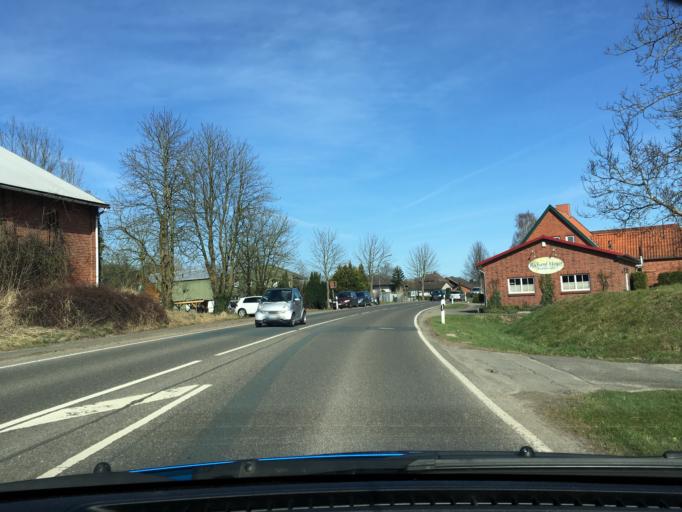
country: DE
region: Schleswig-Holstein
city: Escheburg
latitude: 53.4274
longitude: 10.3079
